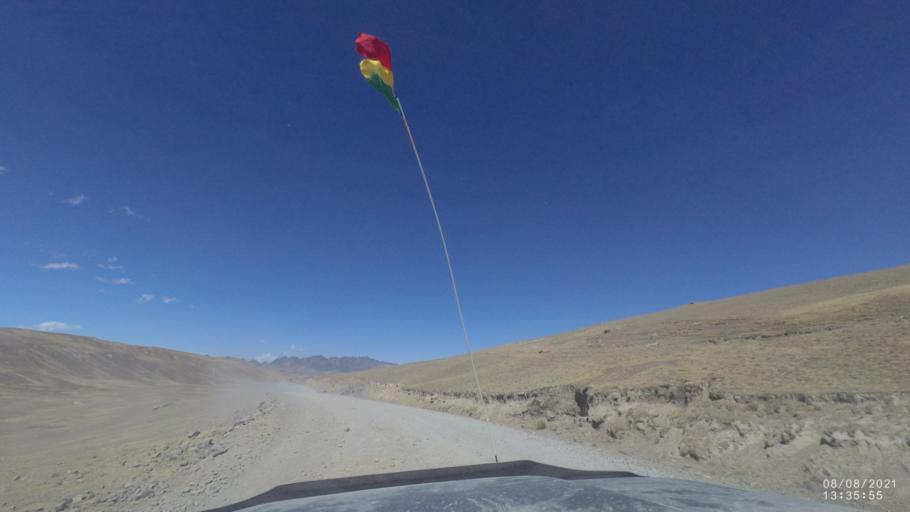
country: BO
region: Cochabamba
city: Colchani
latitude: -17.0700
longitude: -66.5051
